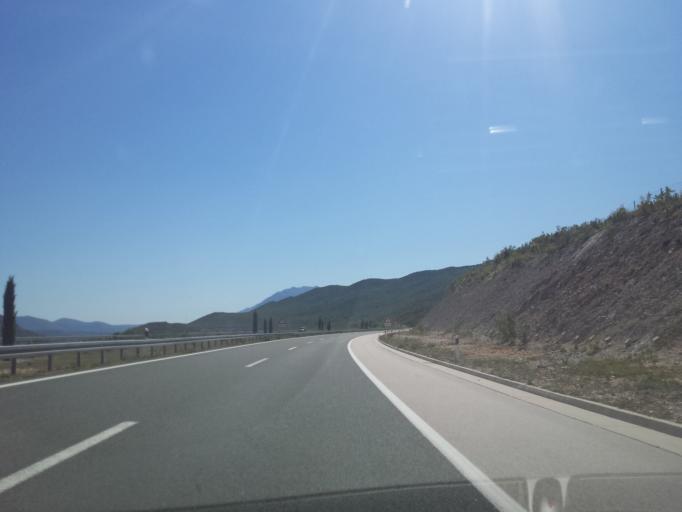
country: HR
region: Splitsko-Dalmatinska
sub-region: Grad Omis
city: Omis
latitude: 43.4906
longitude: 16.7968
